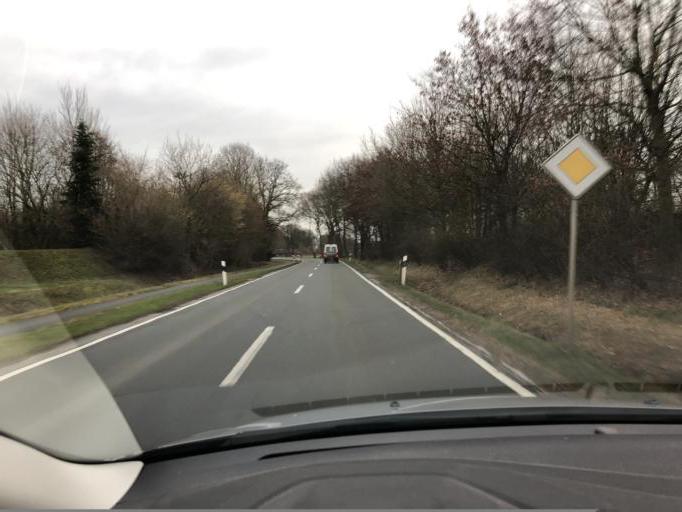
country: DE
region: Lower Saxony
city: Wiefelstede
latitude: 53.1884
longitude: 8.1183
